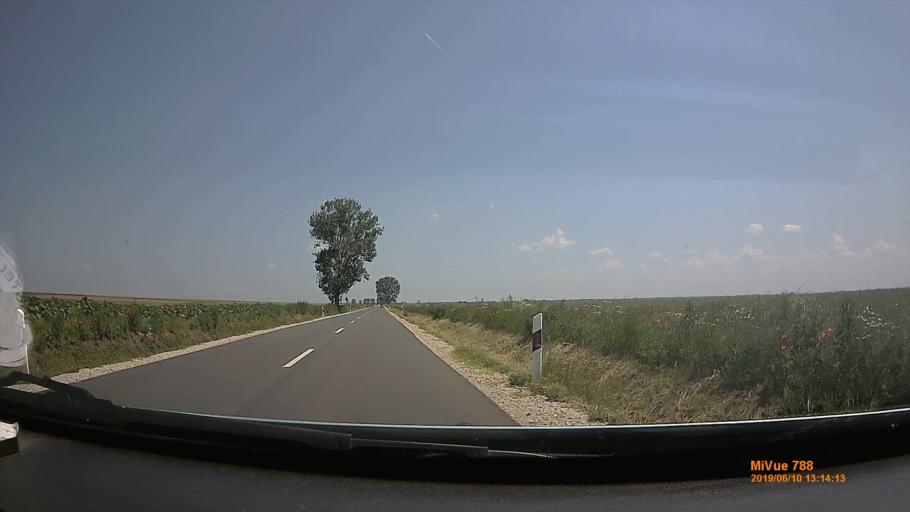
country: HU
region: Borsod-Abauj-Zemplen
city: Hernadnemeti
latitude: 48.0575
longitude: 21.0181
